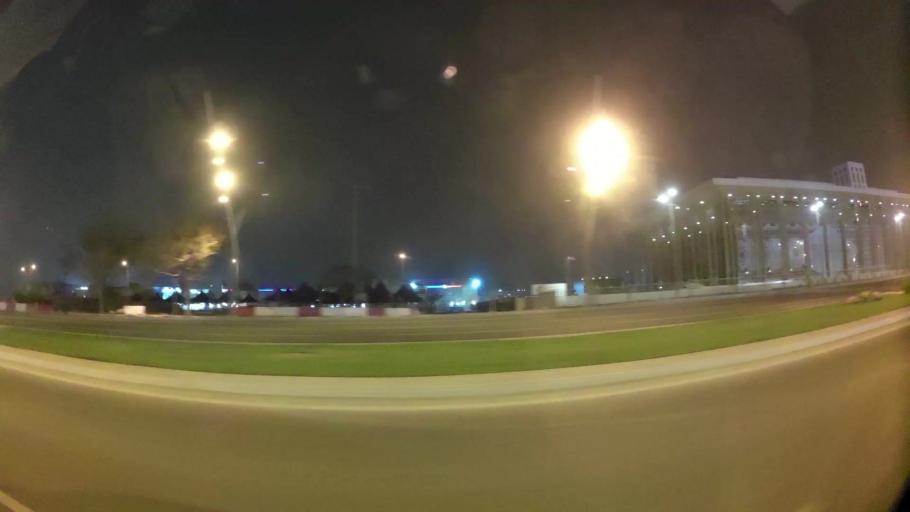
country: QA
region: Baladiyat ar Rayyan
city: Ar Rayyan
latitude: 25.2663
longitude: 51.4513
